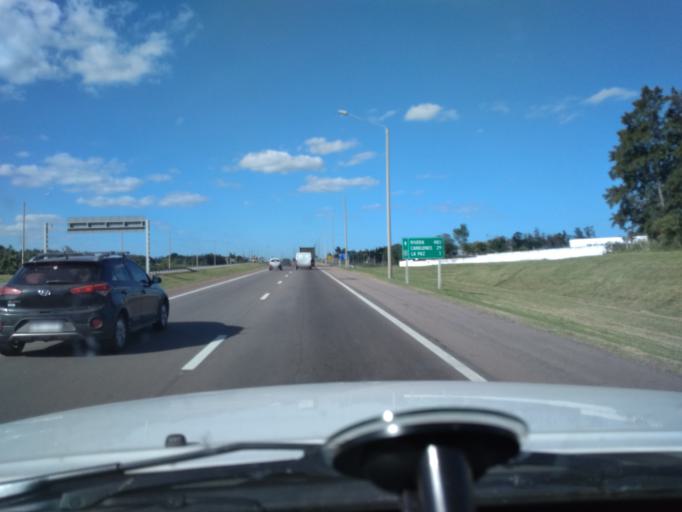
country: UY
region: Canelones
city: La Paz
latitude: -34.7724
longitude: -56.2693
